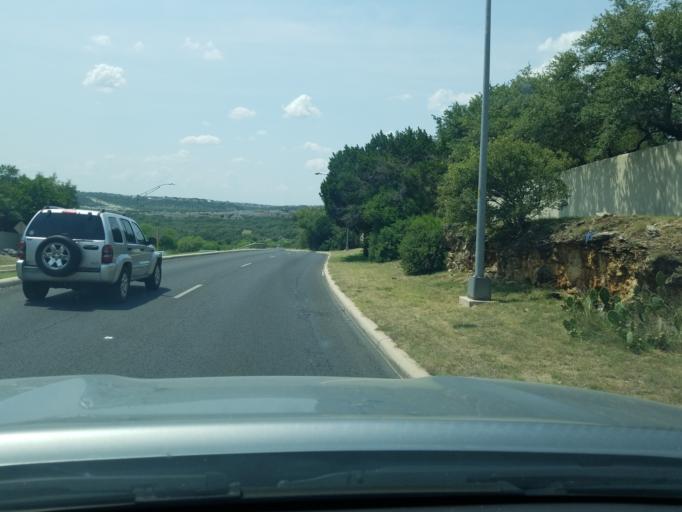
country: US
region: Texas
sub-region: Bexar County
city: Hollywood Park
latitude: 29.6387
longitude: -98.4633
